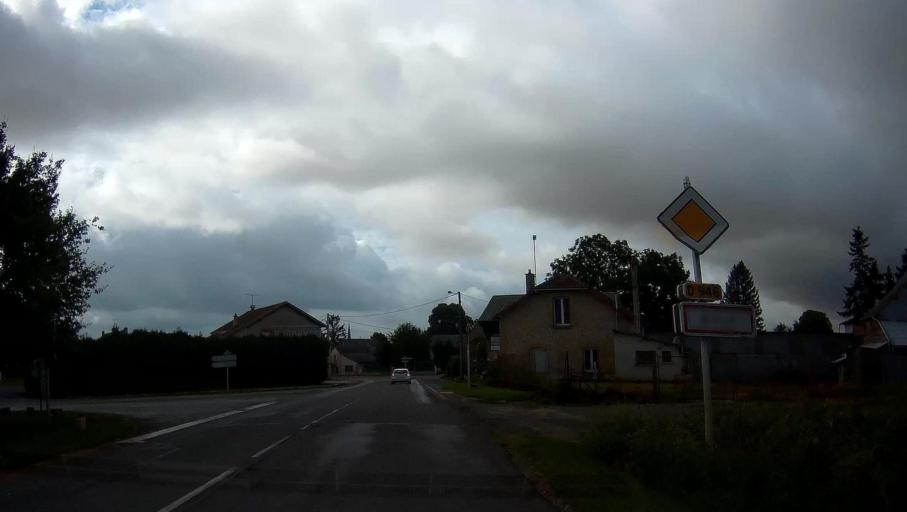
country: FR
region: Champagne-Ardenne
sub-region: Departement des Ardennes
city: Chateau-Porcien
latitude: 49.5465
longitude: 4.2874
